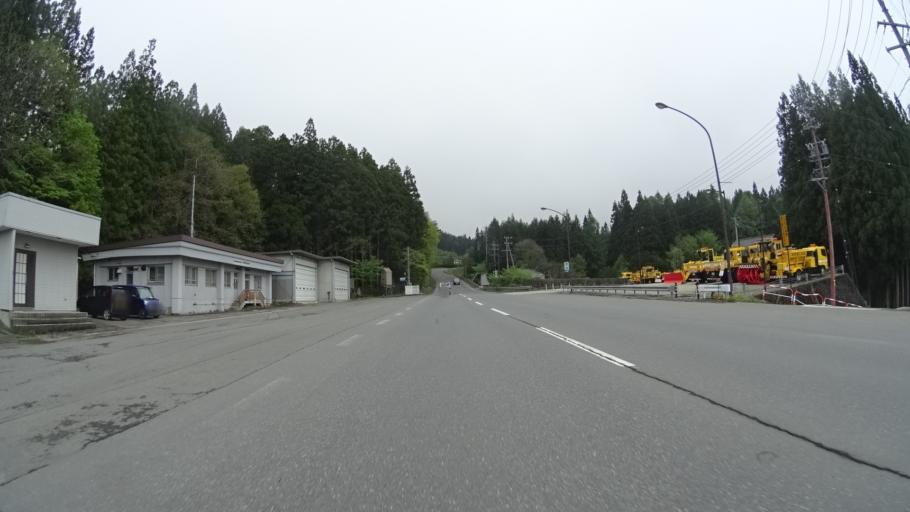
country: JP
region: Nagano
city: Nakano
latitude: 36.7240
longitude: 138.4452
